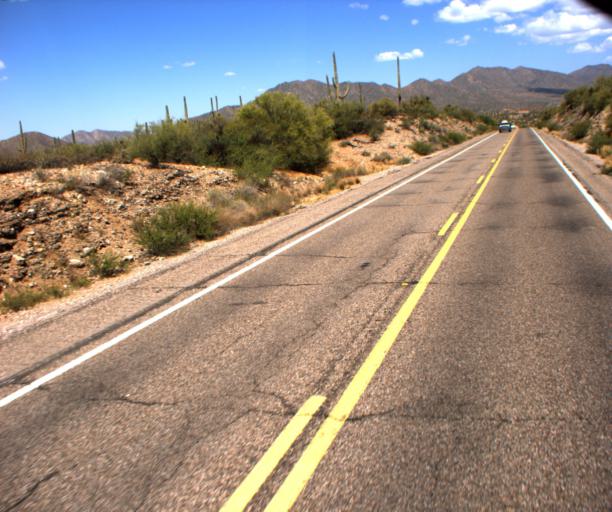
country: US
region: Arizona
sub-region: Pinal County
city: Kearny
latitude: 33.1059
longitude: -110.9456
